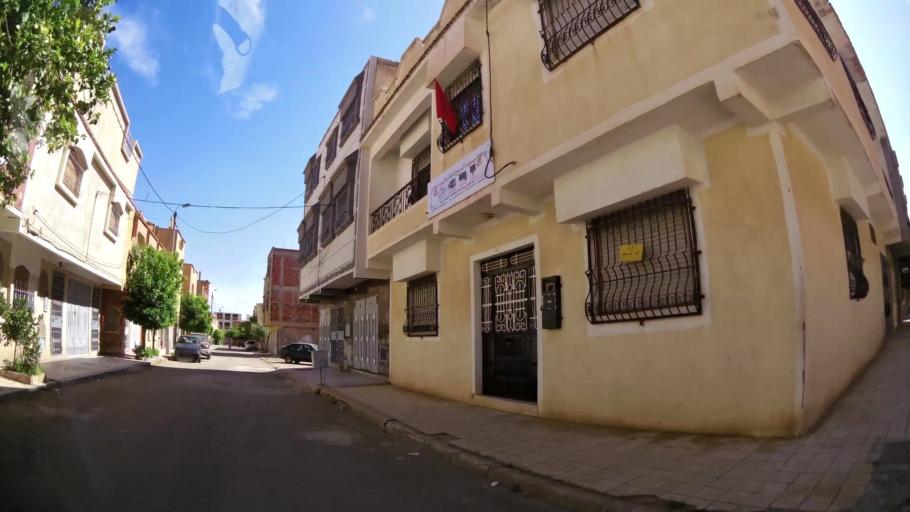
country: MA
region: Oriental
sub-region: Oujda-Angad
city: Oujda
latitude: 34.6536
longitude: -1.9348
